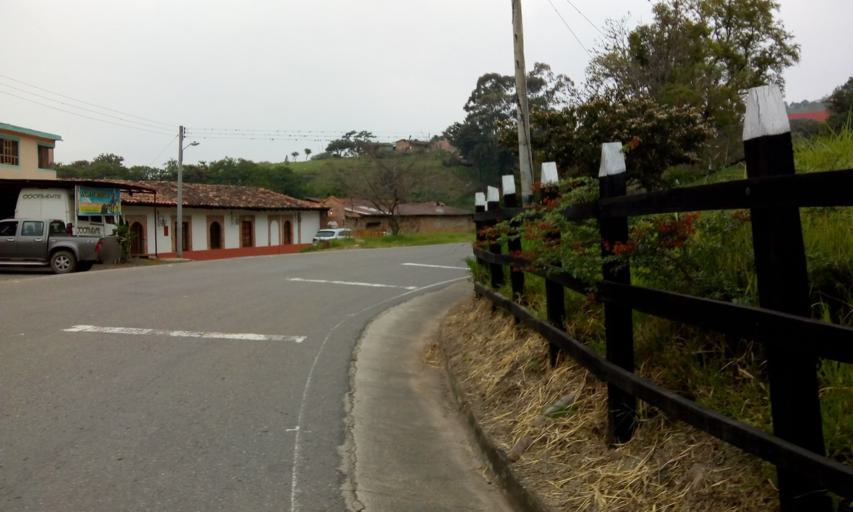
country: CO
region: Boyaca
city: Tipacoque
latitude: 6.4152
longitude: -72.6894
